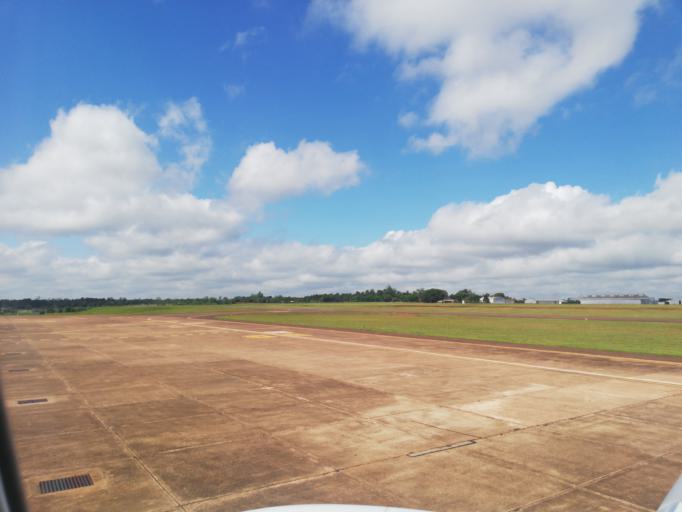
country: AR
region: Misiones
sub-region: Departamento de Capital
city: Posadas
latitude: -27.3912
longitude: -55.9675
